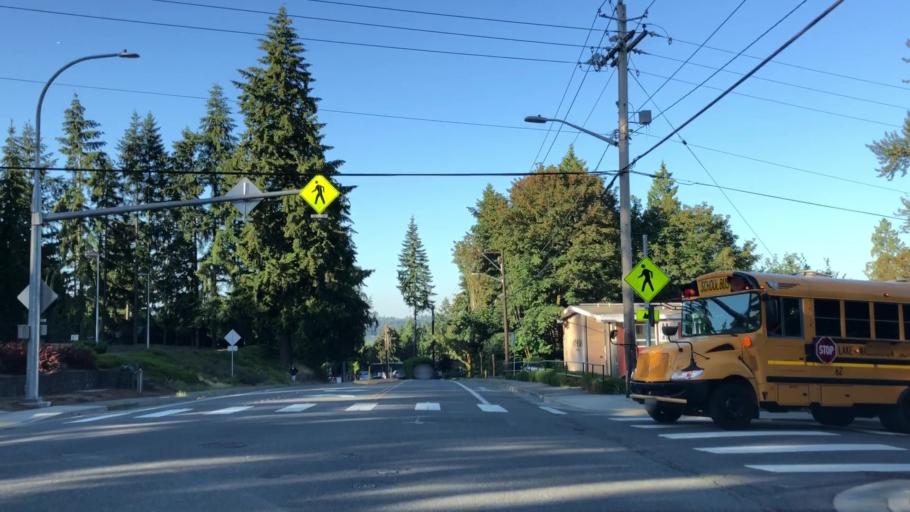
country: US
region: Washington
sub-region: King County
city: Redmond
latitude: 47.6858
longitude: -122.1187
